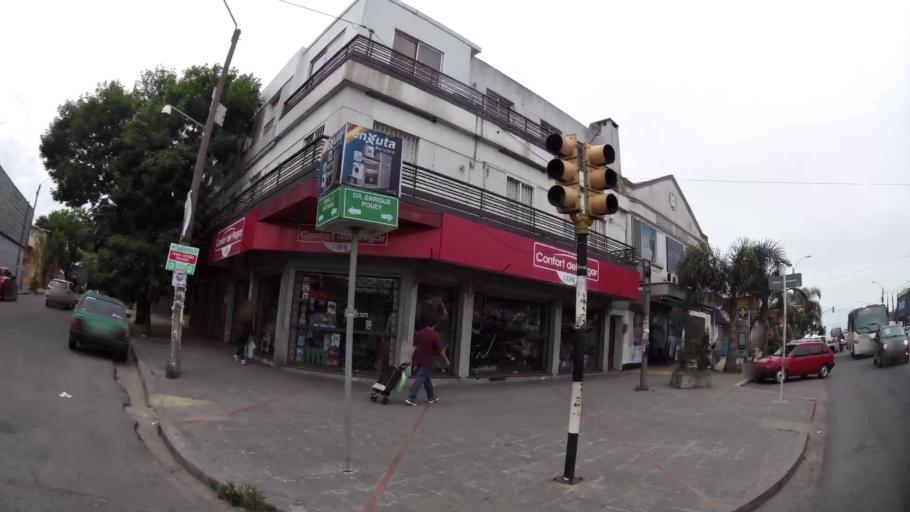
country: UY
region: Canelones
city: Las Piedras
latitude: -34.7274
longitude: -56.2235
